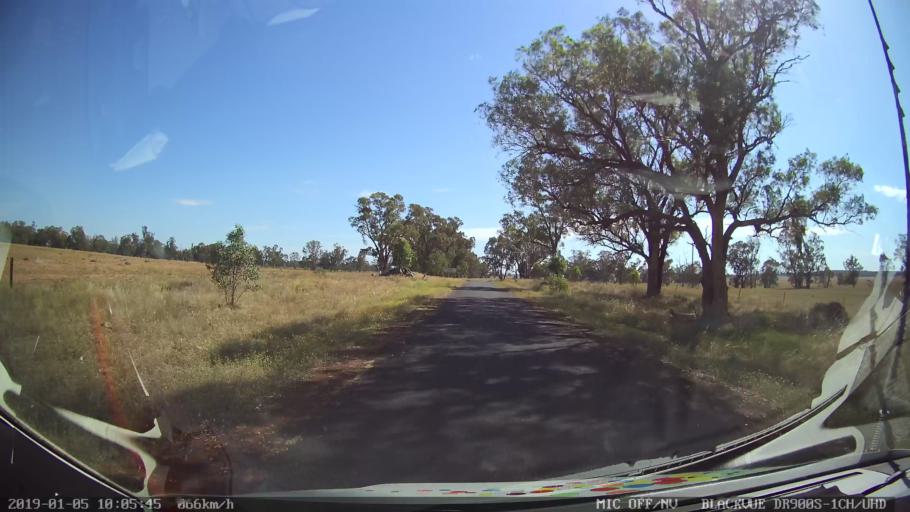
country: AU
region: New South Wales
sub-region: Gilgandra
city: Gilgandra
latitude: -31.6631
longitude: 148.8665
